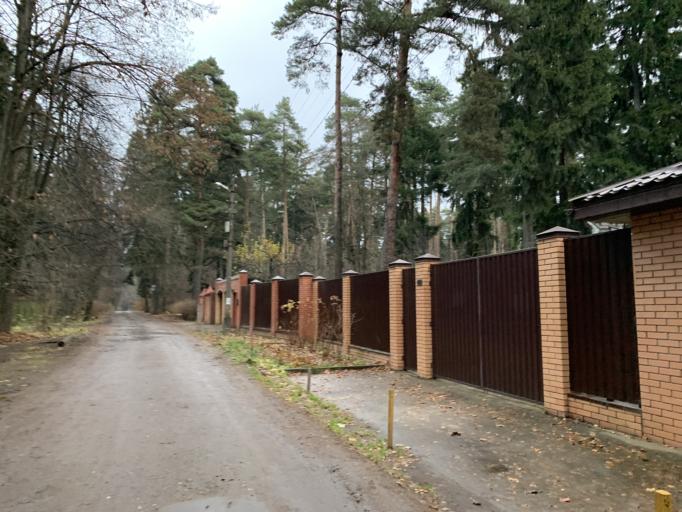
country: RU
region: Moskovskaya
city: Mamontovka
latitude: 55.9858
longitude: 37.8150
